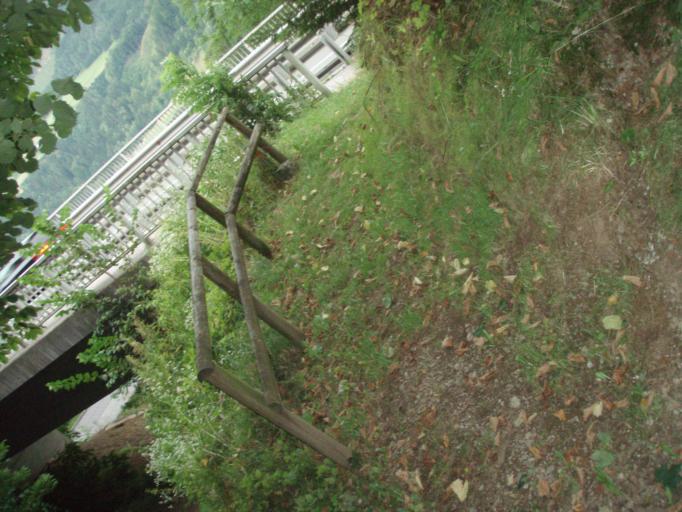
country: AT
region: Salzburg
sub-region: Politischer Bezirk Sankt Johann im Pongau
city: Pfarrwerfen
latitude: 47.4622
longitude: 13.2035
